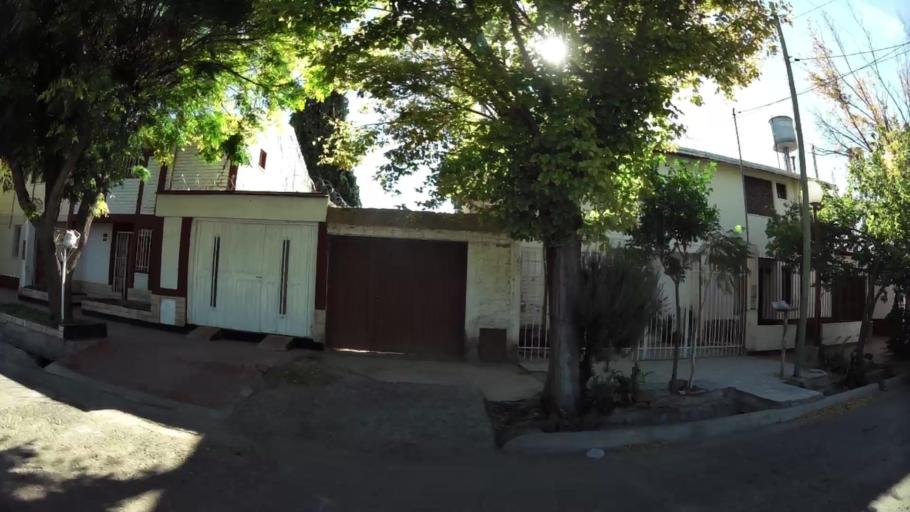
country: AR
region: Mendoza
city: Las Heras
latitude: -32.8498
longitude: -68.8295
